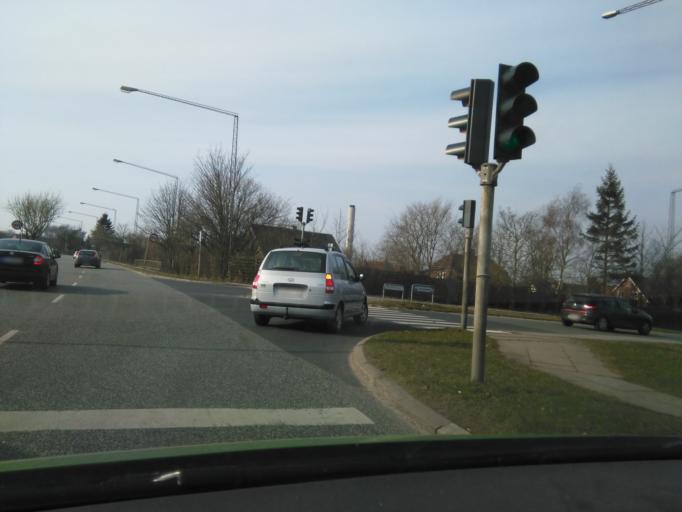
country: DK
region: Central Jutland
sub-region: Arhus Kommune
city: Arhus
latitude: 56.1965
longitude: 10.2183
